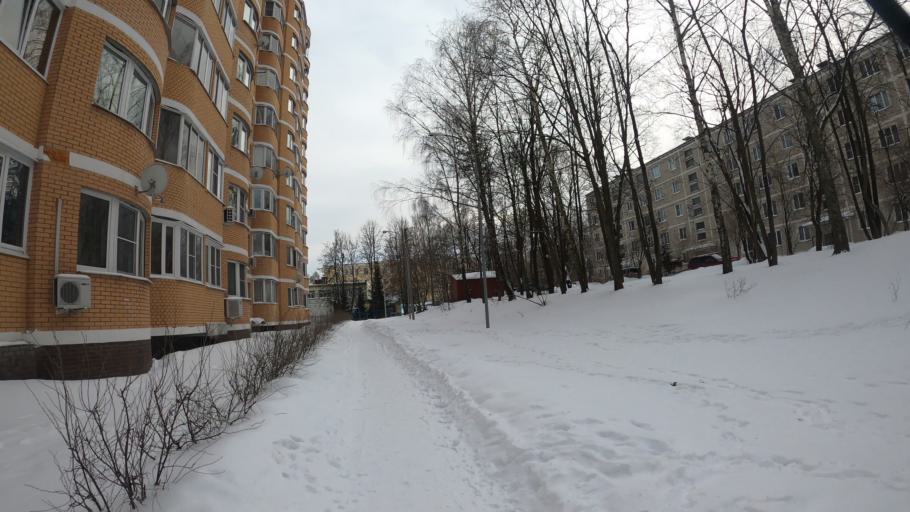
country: RU
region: Moskovskaya
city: Dedenevo
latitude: 56.2372
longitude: 37.5197
